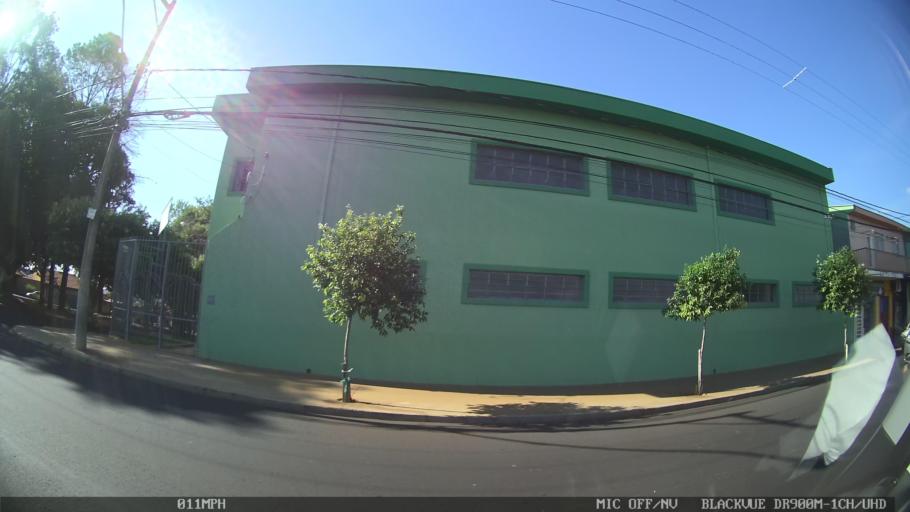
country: BR
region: Sao Paulo
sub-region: Ribeirao Preto
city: Ribeirao Preto
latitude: -21.1865
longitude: -47.7814
